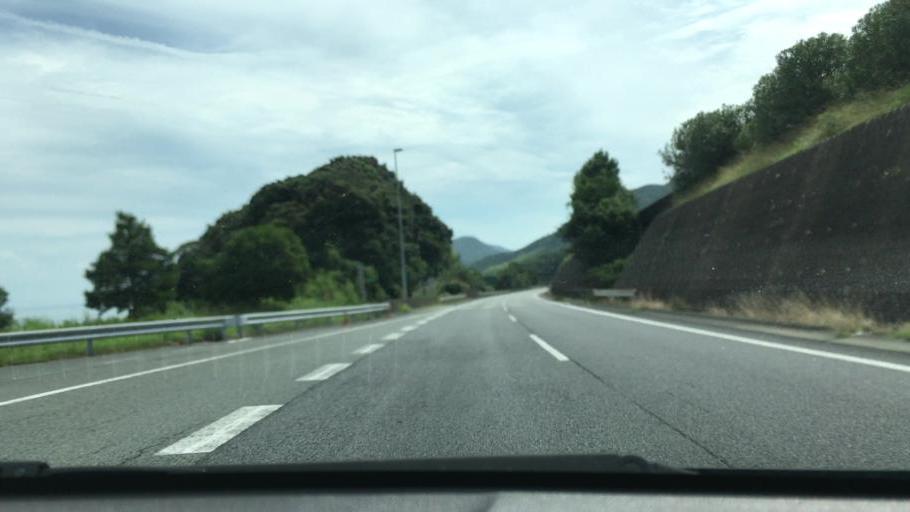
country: JP
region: Yamaguchi
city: Hofu
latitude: 34.0602
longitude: 131.6514
